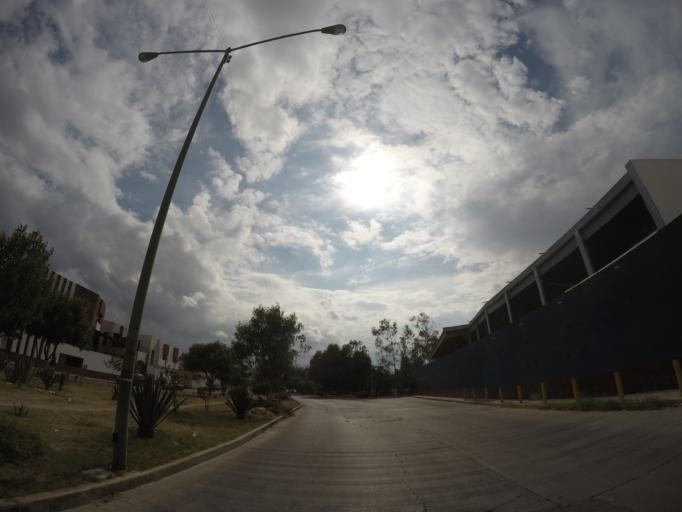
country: MX
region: San Luis Potosi
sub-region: San Luis Potosi
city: San Luis Potosi
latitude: 22.1266
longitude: -100.9784
